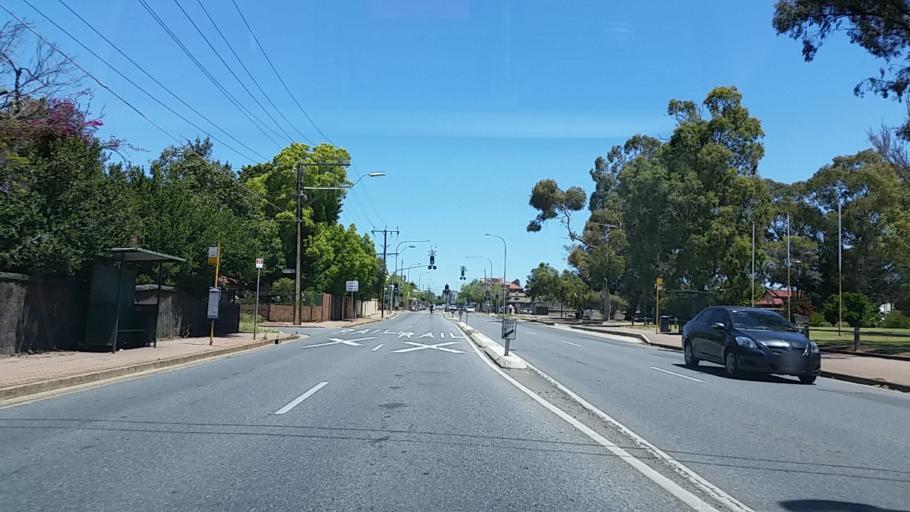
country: AU
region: South Australia
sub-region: Charles Sturt
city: Woodville North
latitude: -34.8766
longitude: 138.5392
